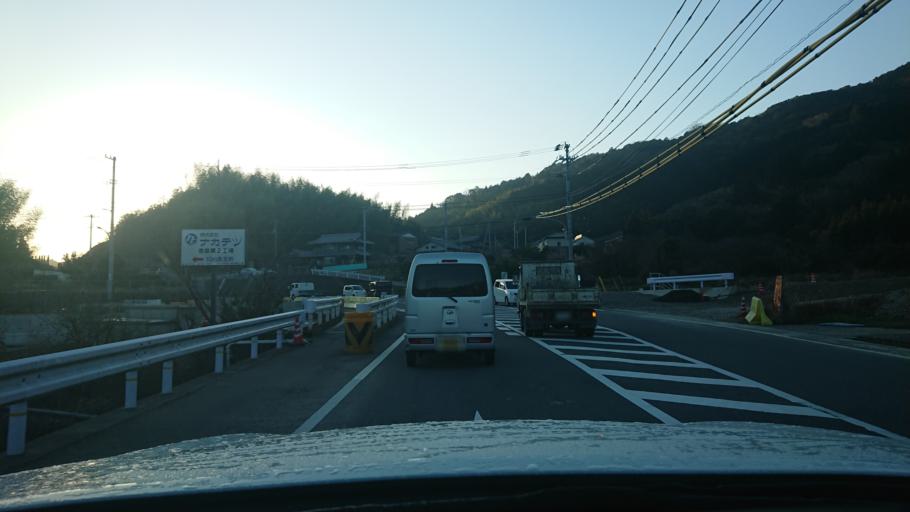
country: JP
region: Tokushima
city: Komatsushimacho
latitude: 33.9491
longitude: 134.5623
